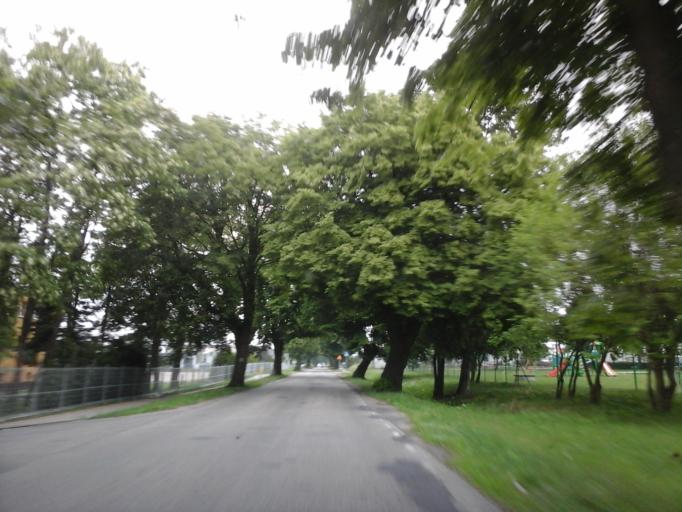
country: PL
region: West Pomeranian Voivodeship
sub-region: Powiat drawski
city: Czaplinek
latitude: 53.5466
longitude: 16.2322
